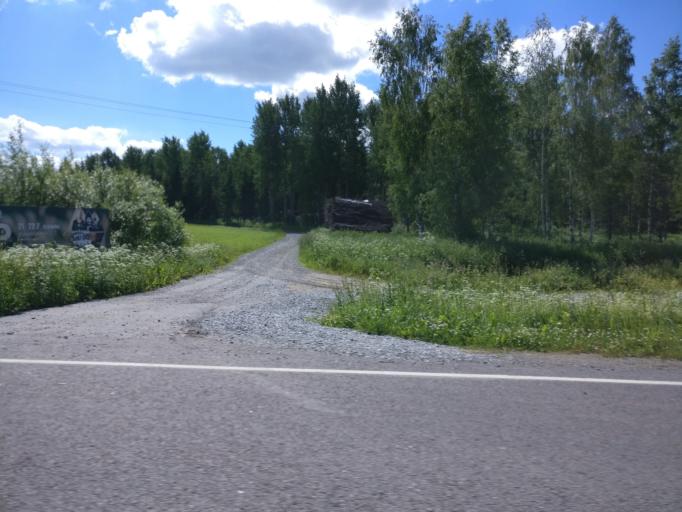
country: FI
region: Southern Savonia
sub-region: Savonlinna
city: Kerimaeki
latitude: 61.8840
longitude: 29.0949
